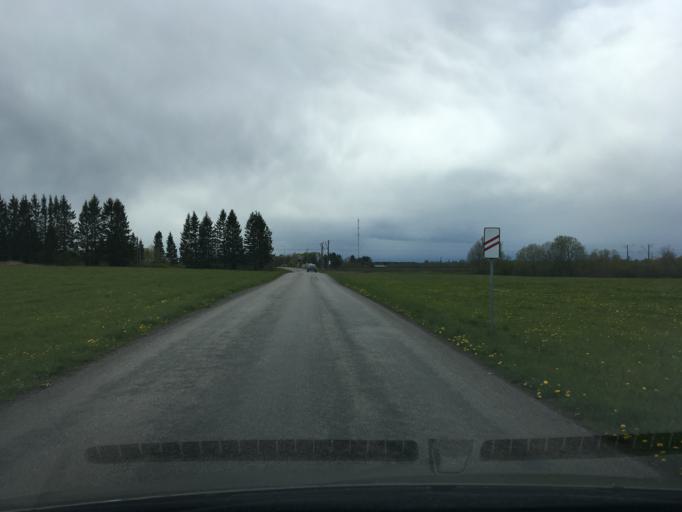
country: EE
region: Harju
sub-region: Joelaehtme vald
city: Loo
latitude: 59.3935
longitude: 24.9641
